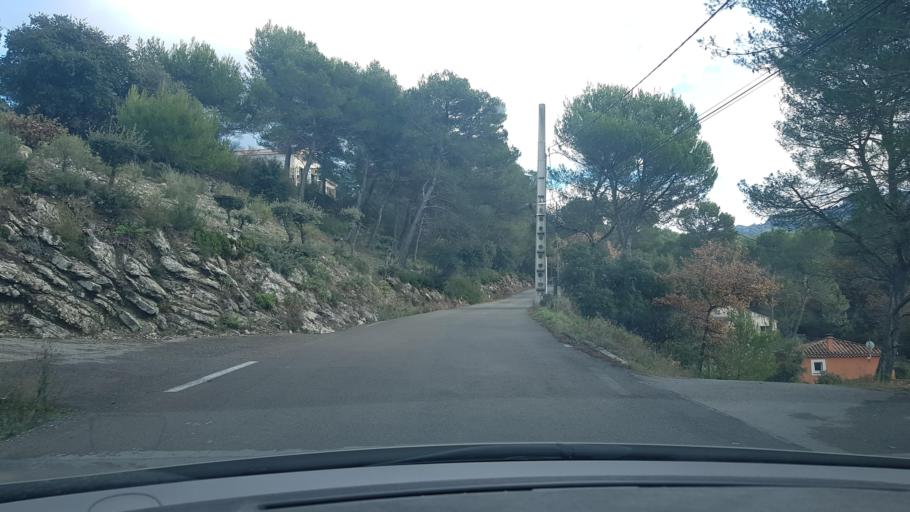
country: FR
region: Provence-Alpes-Cote d'Azur
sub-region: Departement des Bouches-du-Rhone
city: Simiane-Collongue
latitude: 43.4227
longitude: 5.4511
